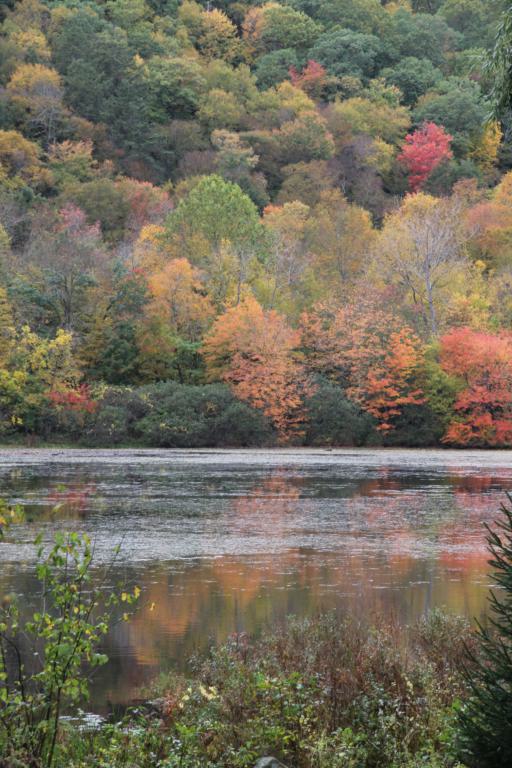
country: US
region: Connecticut
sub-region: Litchfield County
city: Kent
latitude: 41.7656
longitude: -73.5192
